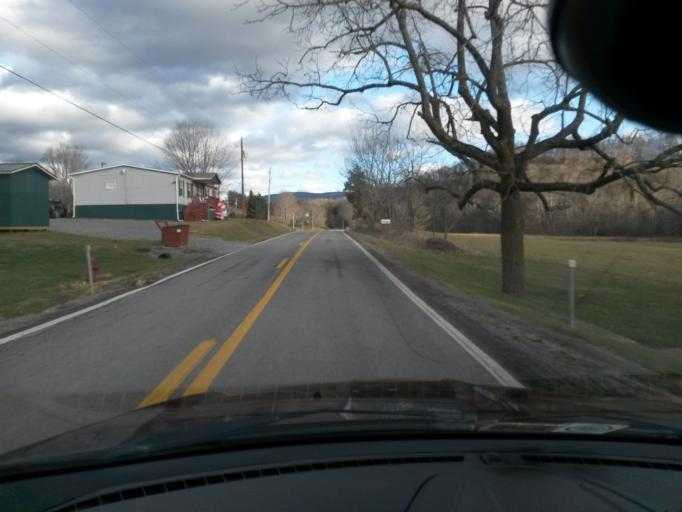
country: US
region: West Virginia
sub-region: Monroe County
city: Union
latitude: 37.4779
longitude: -80.6503
